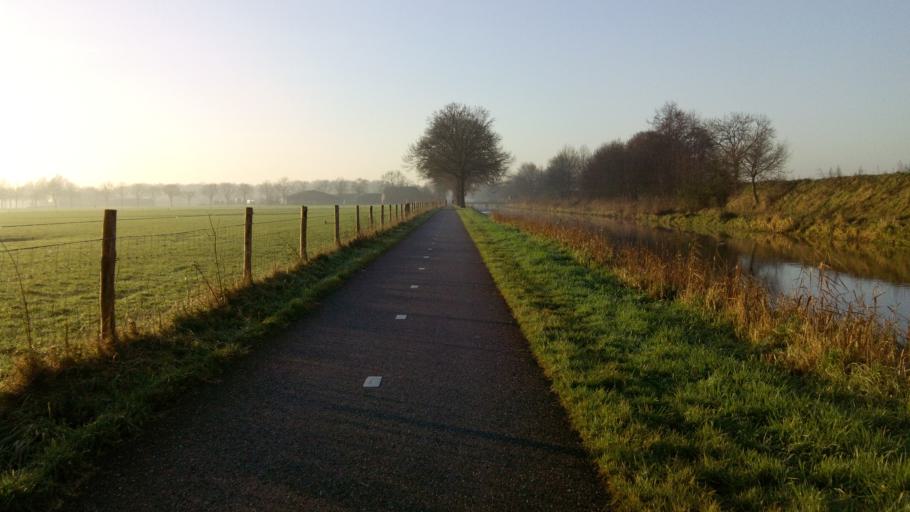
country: NL
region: Utrecht
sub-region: Gemeente Leusden
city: Leusden
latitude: 52.1183
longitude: 5.4432
